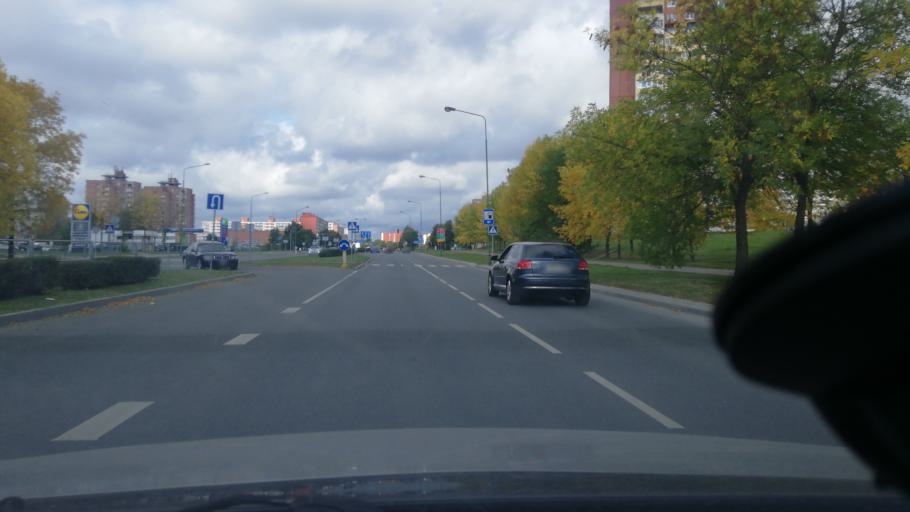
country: LT
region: Klaipedos apskritis
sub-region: Klaipeda
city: Klaipeda
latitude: 55.6687
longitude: 21.1945
